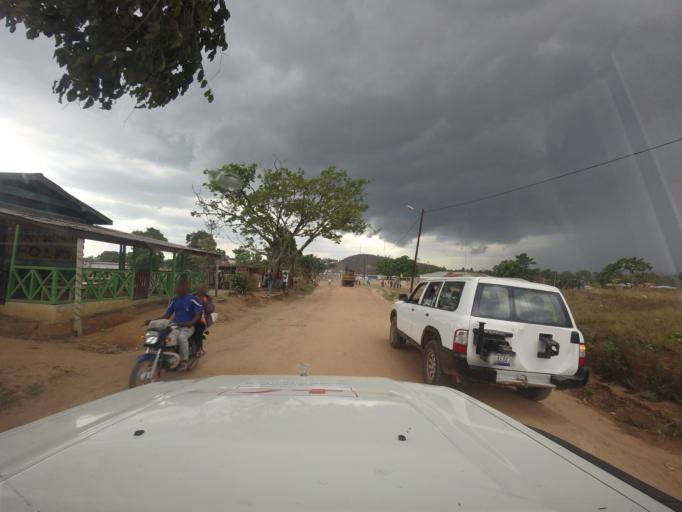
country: LR
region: Lofa
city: Voinjama
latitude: 8.4199
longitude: -9.7470
